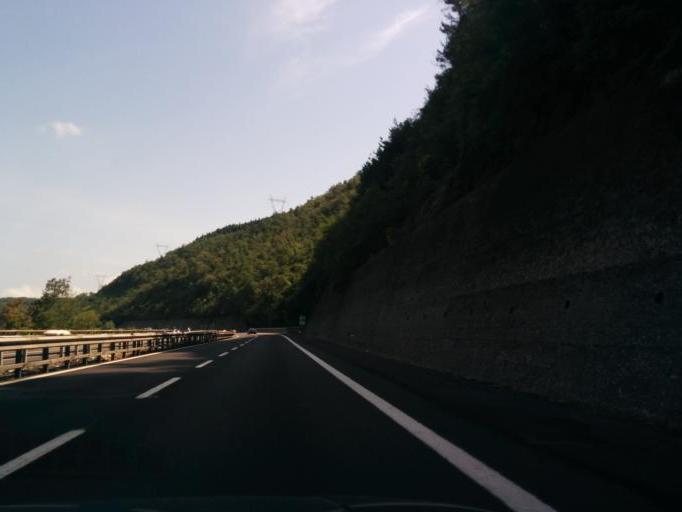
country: IT
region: Tuscany
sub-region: Province of Florence
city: Carraia
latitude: 43.9253
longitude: 11.2165
